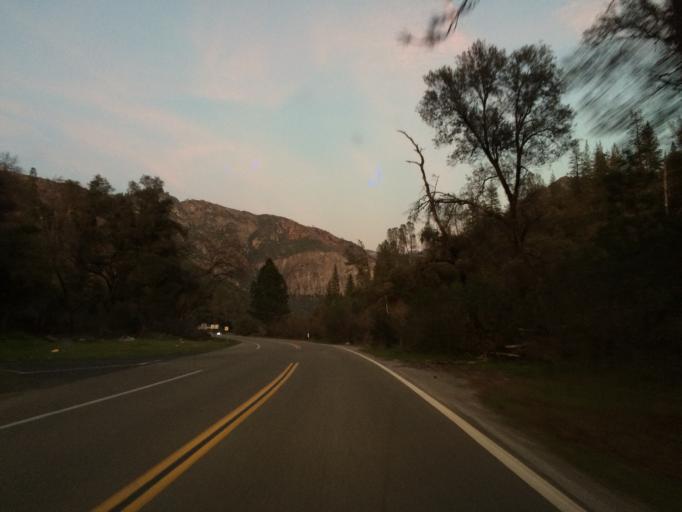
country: US
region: California
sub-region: Mariposa County
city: Midpines
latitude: 37.6729
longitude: -119.7860
